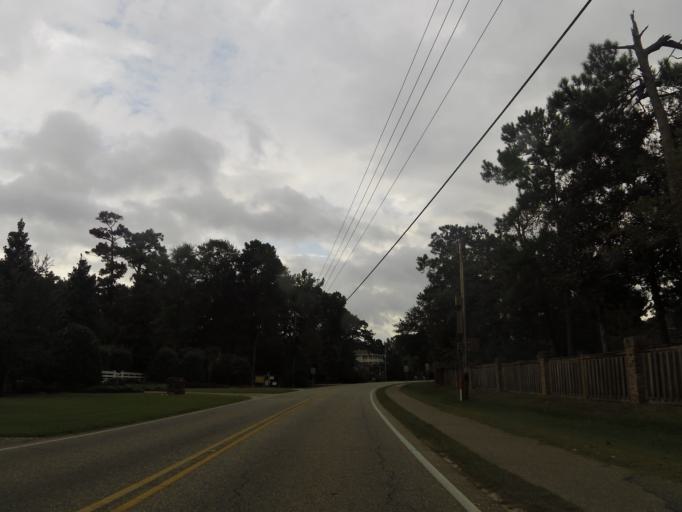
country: US
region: Alabama
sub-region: Baldwin County
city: Point Clear
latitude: 30.4870
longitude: -87.9318
